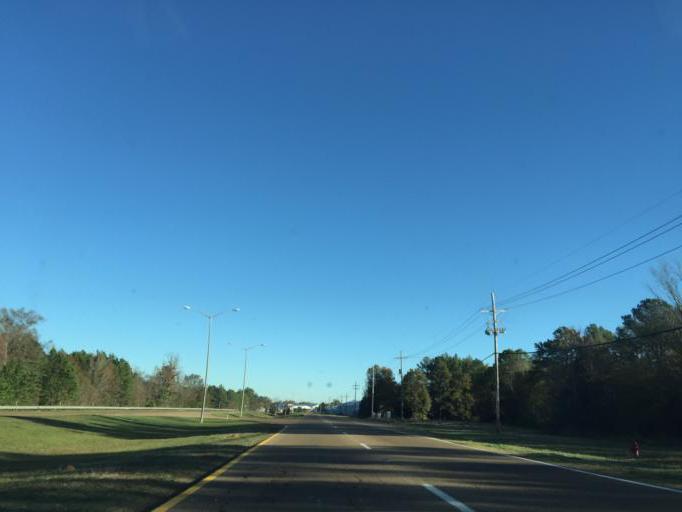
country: US
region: Mississippi
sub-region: Rankin County
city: Flowood
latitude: 32.2952
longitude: -90.1445
